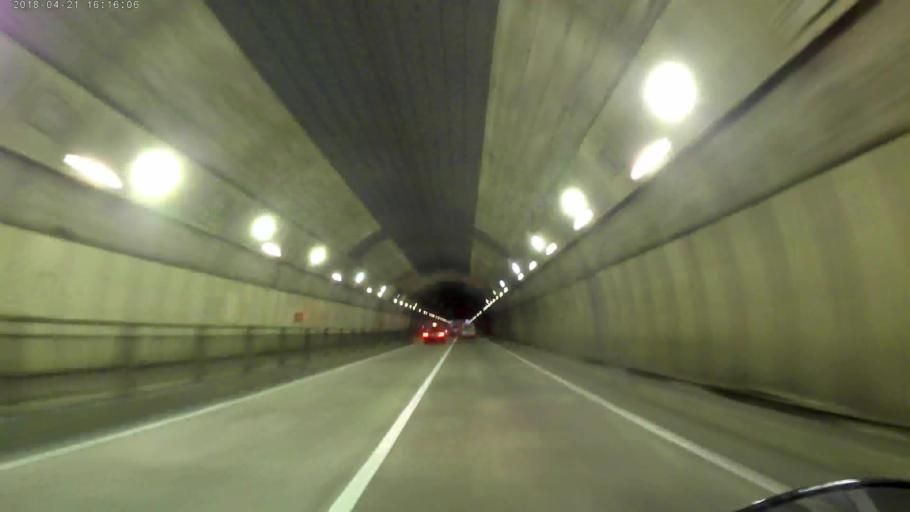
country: JP
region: Kanagawa
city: Fujisawa
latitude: 35.3490
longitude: 139.4464
